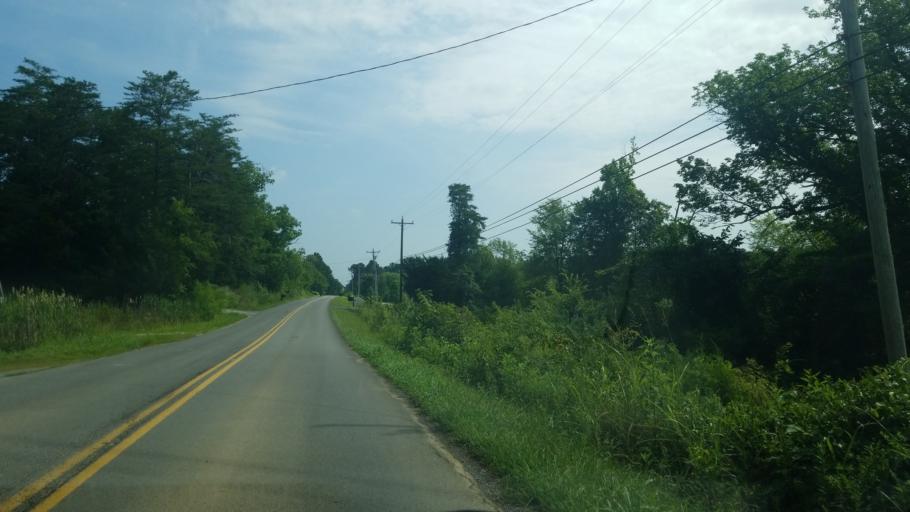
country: US
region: Tennessee
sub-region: Hamilton County
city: Apison
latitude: 35.0581
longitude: -84.9838
